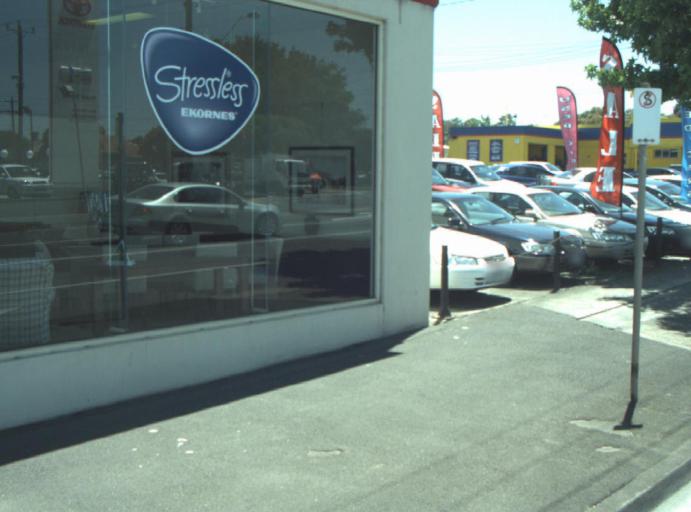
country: AU
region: Victoria
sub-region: Greater Geelong
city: Geelong
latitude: -38.1621
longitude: 144.3539
